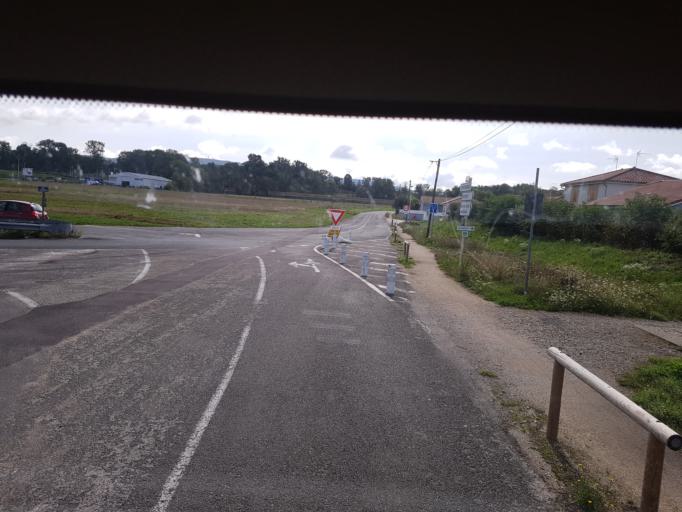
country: FR
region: Rhone-Alpes
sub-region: Departement de l'Ain
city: Montagnat
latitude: 46.1949
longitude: 5.2648
